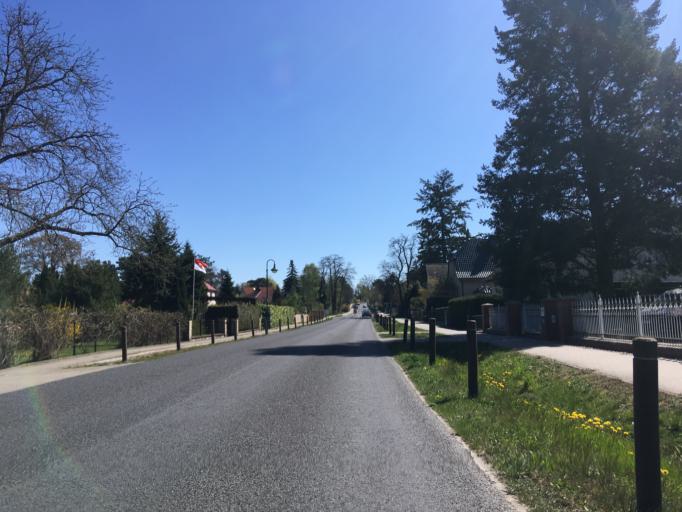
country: DE
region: Brandenburg
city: Bernau bei Berlin
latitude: 52.6465
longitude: 13.5523
